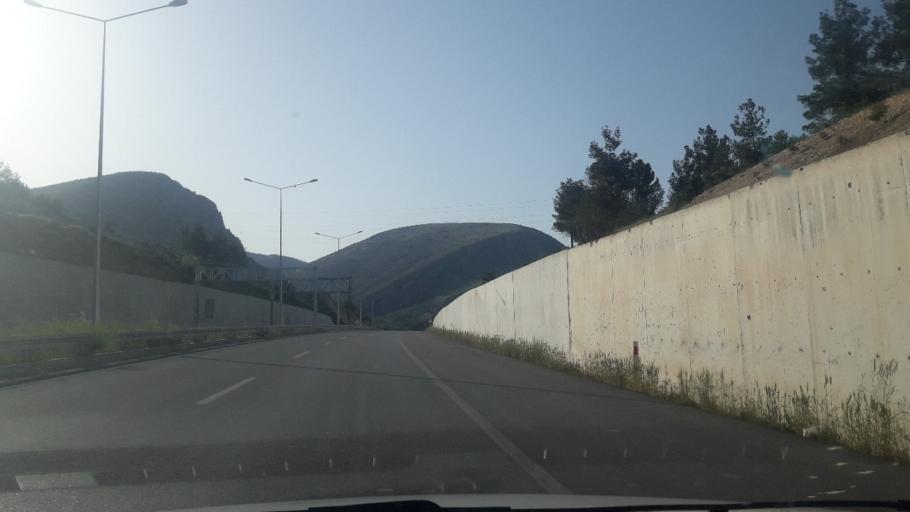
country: TR
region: Amasya
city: Amasya
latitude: 40.6452
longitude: 35.7907
